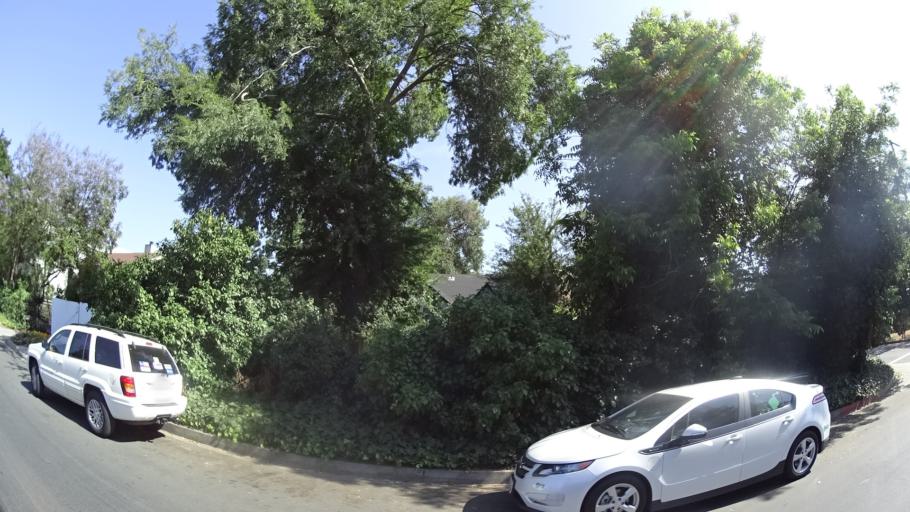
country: US
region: California
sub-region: Los Angeles County
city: Sherman Oaks
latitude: 34.1612
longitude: -118.4549
